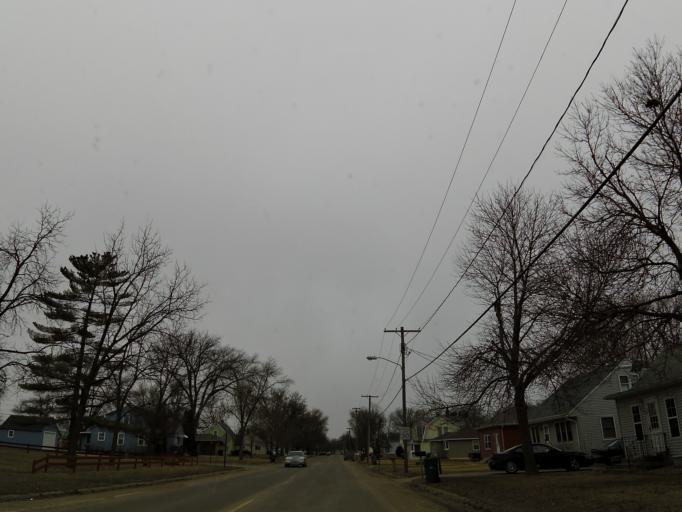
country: US
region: Minnesota
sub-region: Le Sueur County
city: Le Sueur
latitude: 44.4675
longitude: -93.9067
